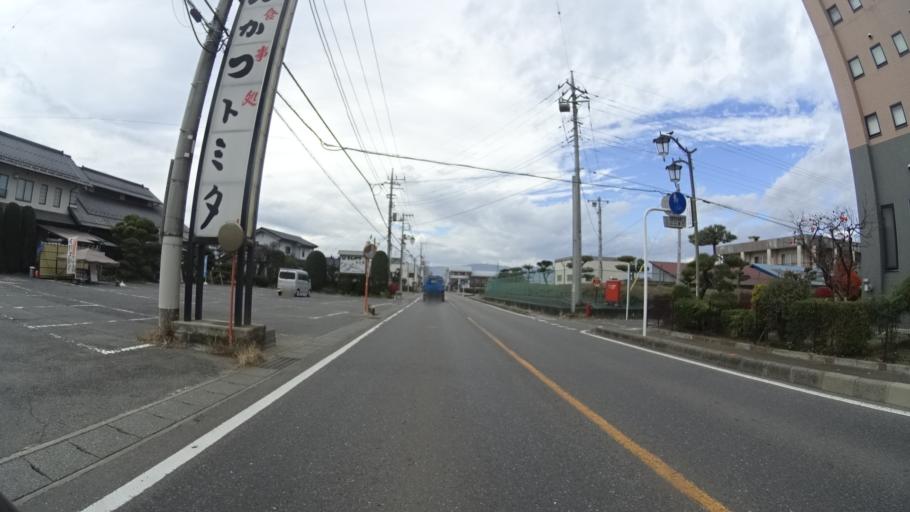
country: JP
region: Gunma
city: Numata
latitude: 36.6588
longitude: 139.0854
